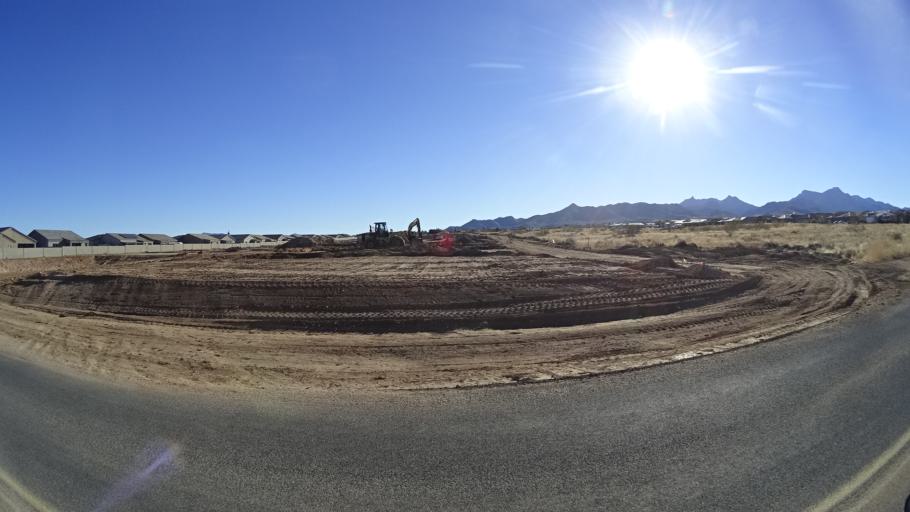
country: US
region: Arizona
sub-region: Mohave County
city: Kingman
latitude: 35.1898
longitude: -114.0030
